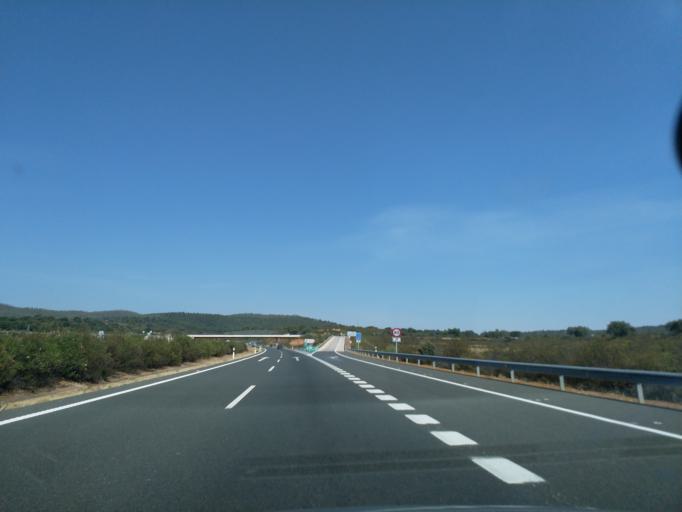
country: ES
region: Extremadura
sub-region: Provincia de Caceres
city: Alcuescar
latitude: 39.1419
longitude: -6.2741
